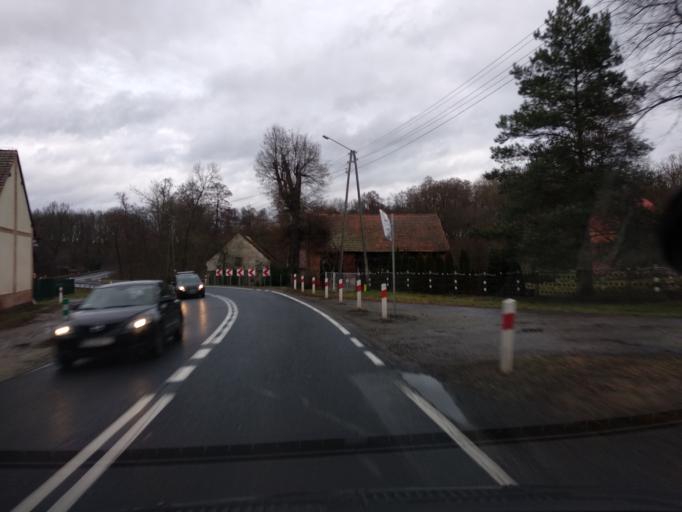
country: PL
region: Lower Silesian Voivodeship
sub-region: Powiat olesnicki
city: Olesnica
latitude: 51.2481
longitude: 17.4744
